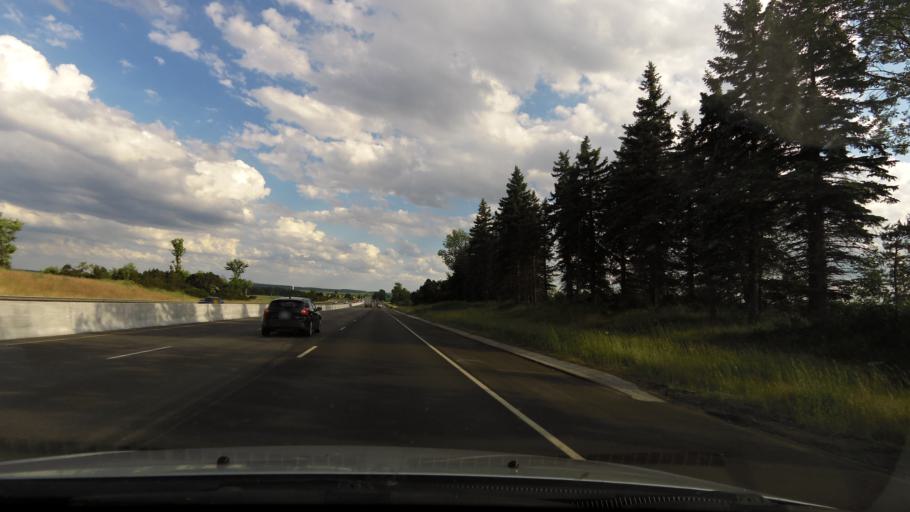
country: CA
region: Ontario
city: Innisfil
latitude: 44.2172
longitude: -79.6615
